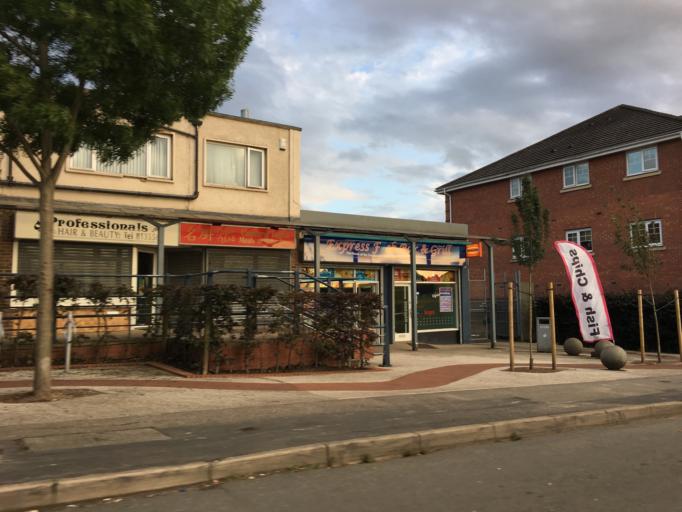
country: GB
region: England
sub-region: Warwickshire
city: Rugby
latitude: 52.3593
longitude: -1.2780
